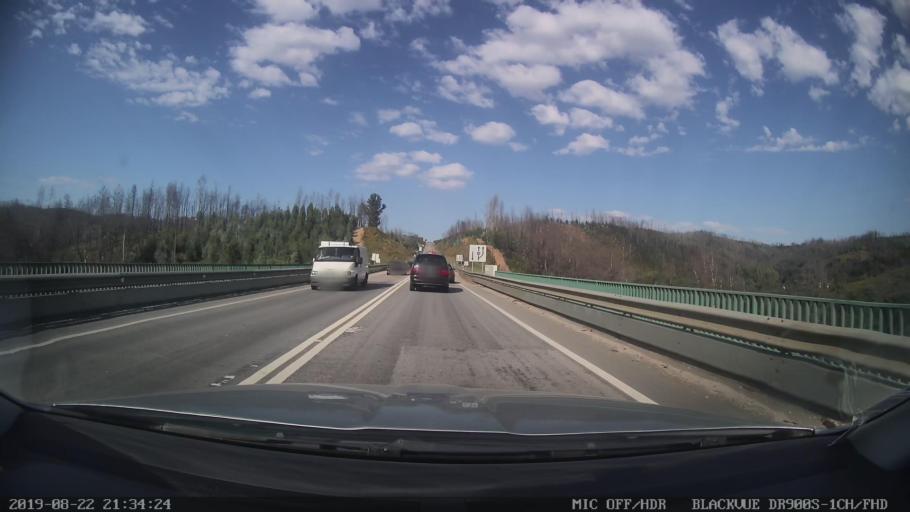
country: PT
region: Leiria
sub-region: Pedrogao Grande
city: Pedrogao Grande
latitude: 39.9271
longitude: -8.1913
